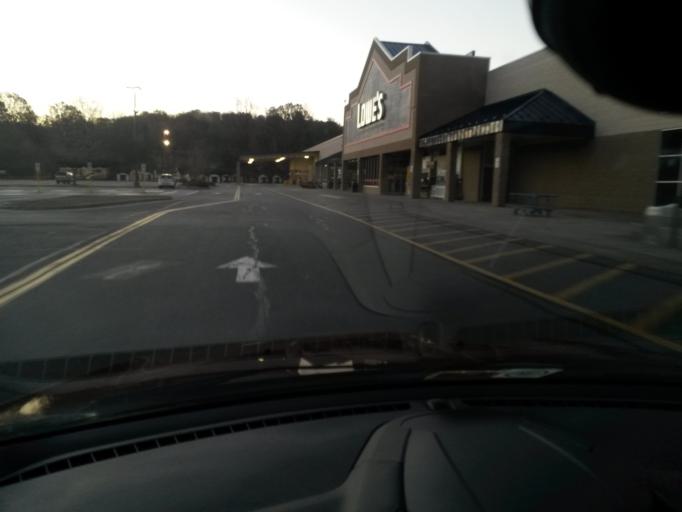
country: US
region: Virginia
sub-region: Roanoke County
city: Narrows
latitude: 37.2246
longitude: -79.9716
